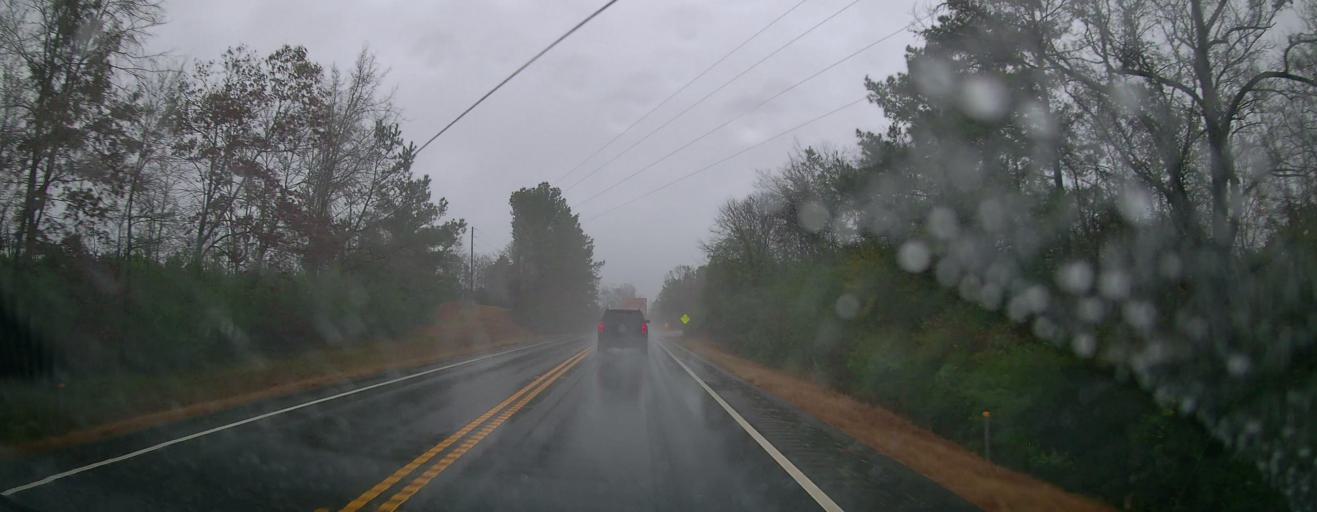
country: US
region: Georgia
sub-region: Putnam County
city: Eatonton
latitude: 33.2673
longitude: -83.4139
